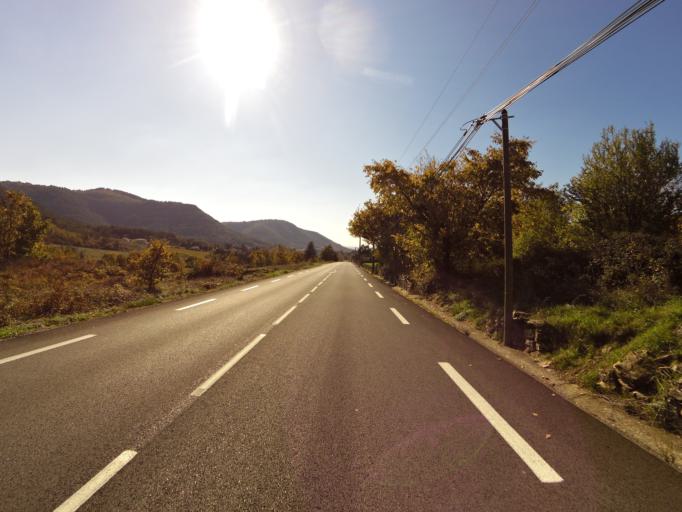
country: FR
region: Rhone-Alpes
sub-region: Departement de l'Ardeche
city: Vesseaux
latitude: 44.6637
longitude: 4.4521
